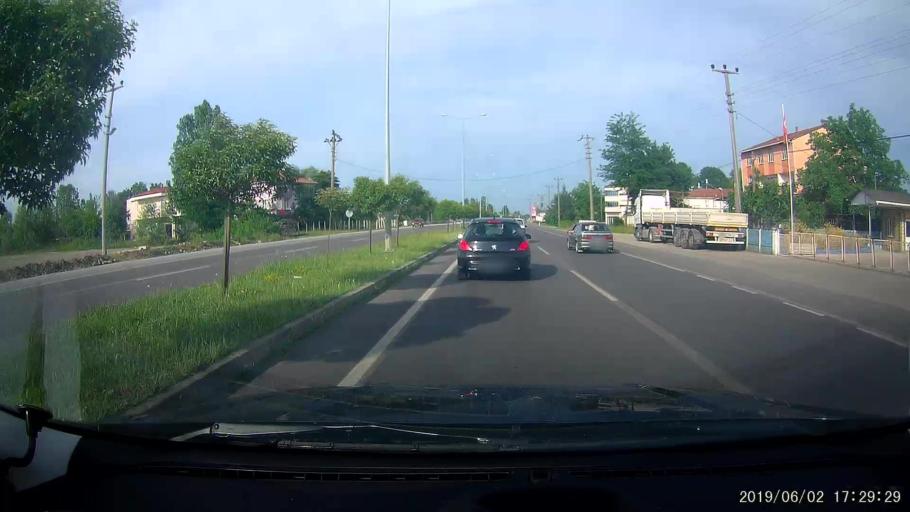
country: TR
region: Samsun
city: Carsamba
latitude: 41.2119
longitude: 36.7605
